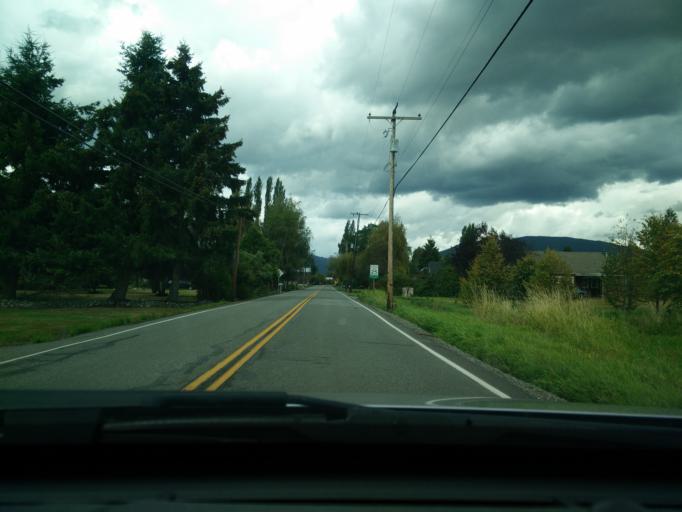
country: US
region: Washington
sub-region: Skagit County
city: Burlington
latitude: 48.5584
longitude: -122.4443
